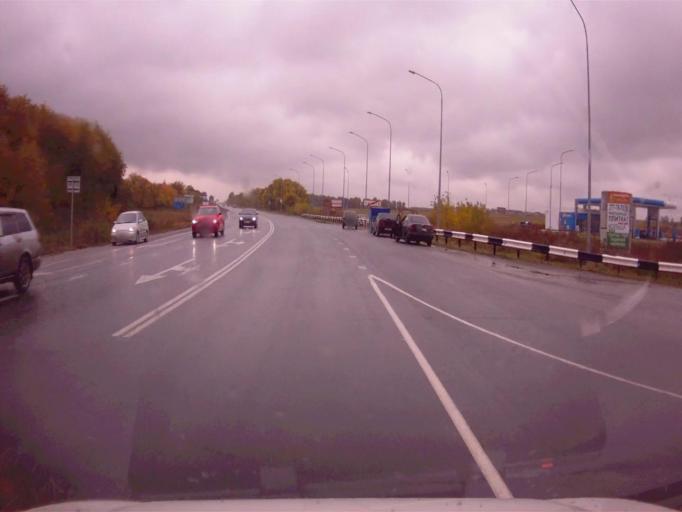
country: RU
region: Chelyabinsk
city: Roshchino
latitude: 55.3695
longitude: 61.1828
